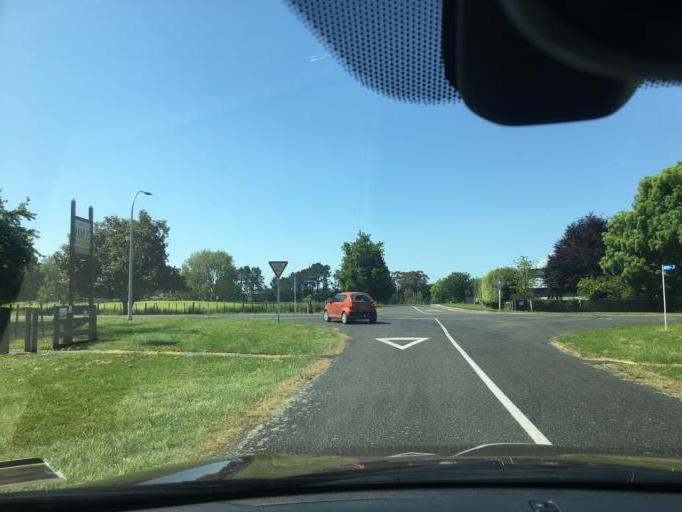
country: NZ
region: Waikato
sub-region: Waipa District
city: Cambridge
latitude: -37.9159
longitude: 175.4625
